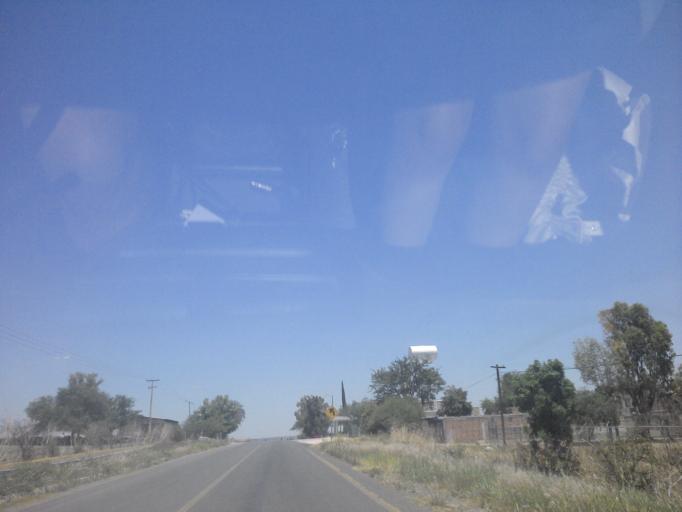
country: MX
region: Guanajuato
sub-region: San Francisco del Rincon
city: San Ignacio de Hidalgo
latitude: 20.8915
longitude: -101.9378
